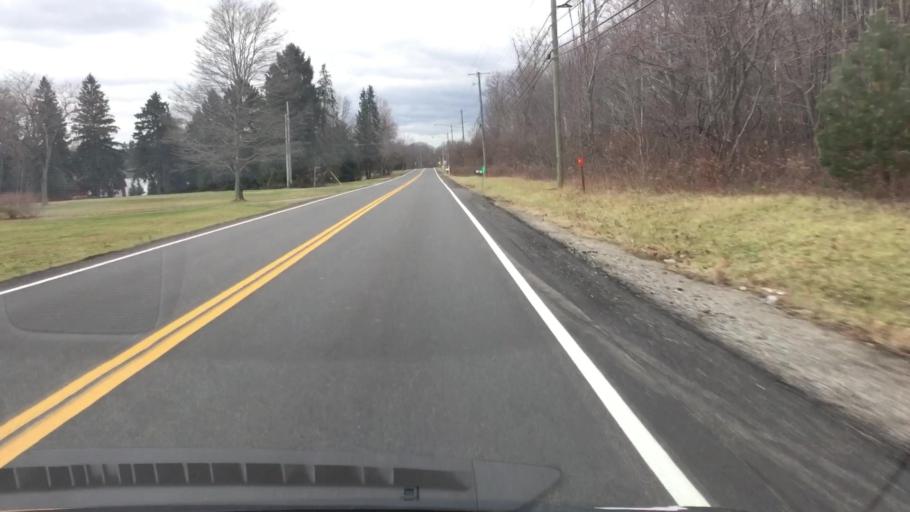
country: US
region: Ohio
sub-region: Summit County
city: Boston Heights
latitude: 41.2594
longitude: -81.5106
